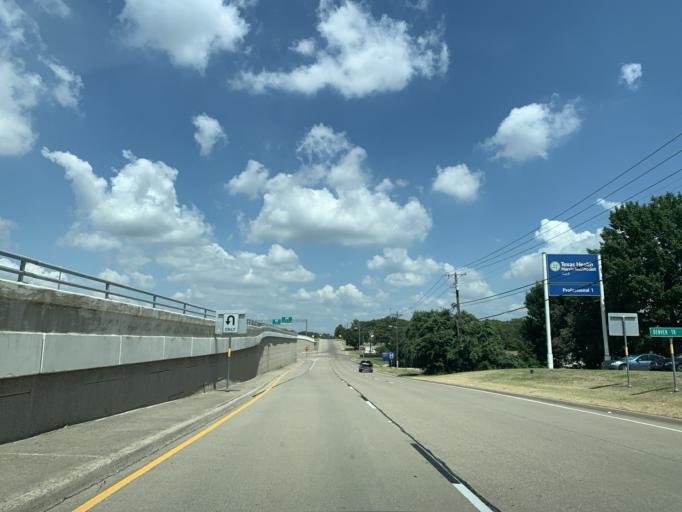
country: US
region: Texas
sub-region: Tarrant County
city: Azle
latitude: 32.8792
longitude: -97.5333
